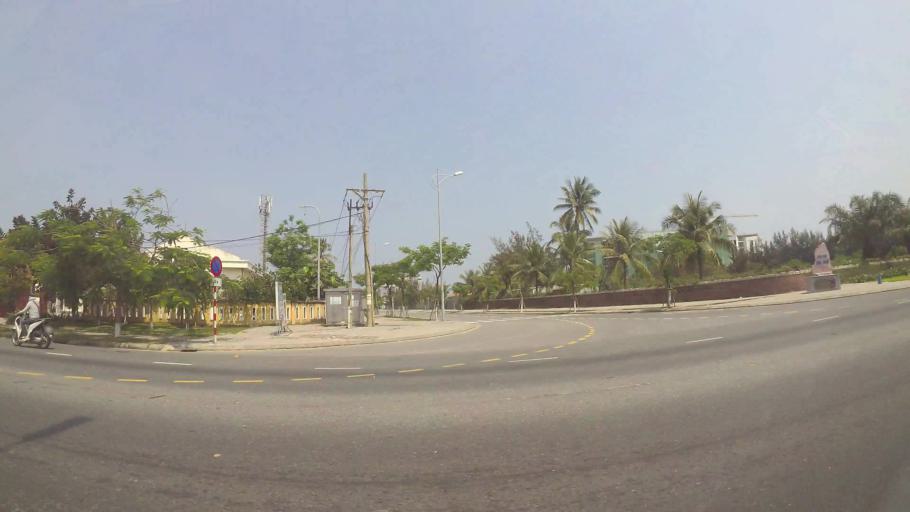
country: VN
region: Da Nang
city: Ngu Hanh Son
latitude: 16.0014
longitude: 108.2672
